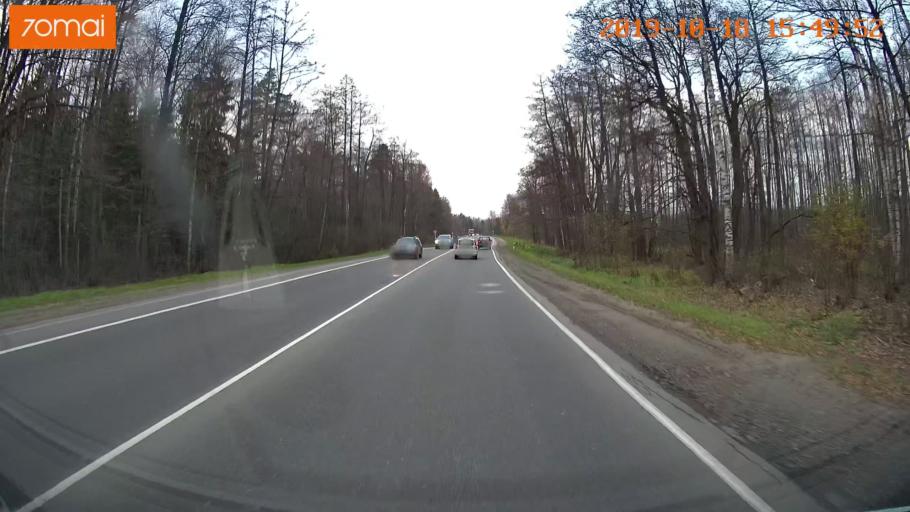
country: RU
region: Vladimir
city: Kommunar
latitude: 56.0275
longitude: 40.5683
